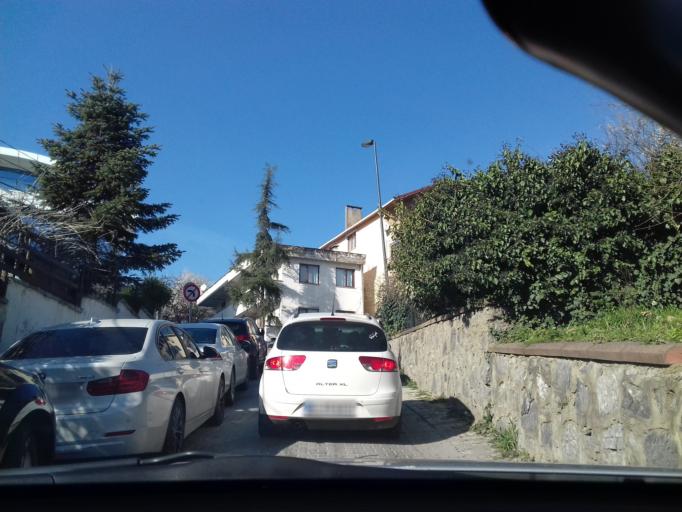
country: TR
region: Istanbul
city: UEskuedar
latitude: 41.0211
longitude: 29.0694
